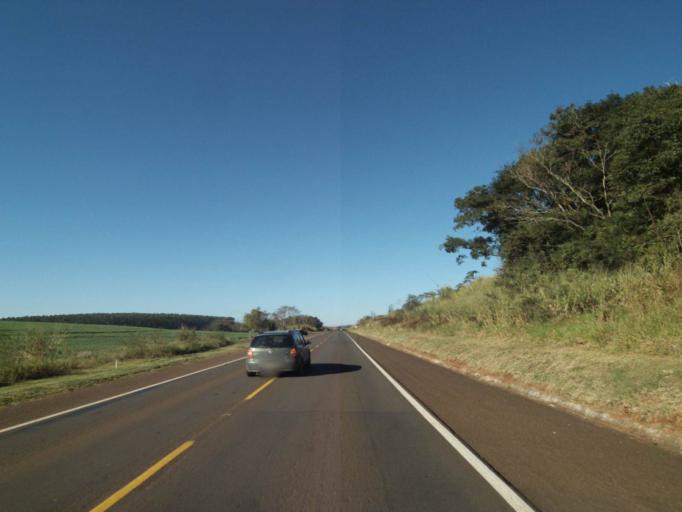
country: BR
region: Parana
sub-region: Londrina
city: Londrina
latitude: -23.5594
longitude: -51.1186
